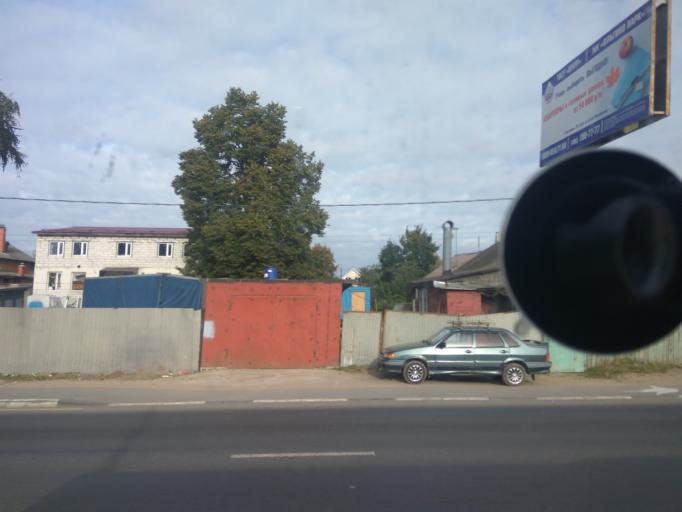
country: RU
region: Moscow
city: Vostochnyy
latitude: 55.8162
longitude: 37.8467
